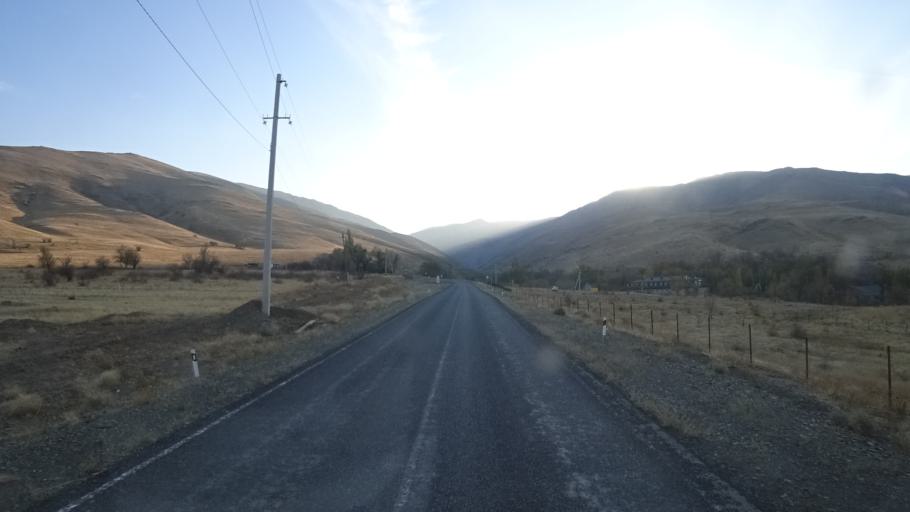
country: KZ
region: Zhambyl
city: Karatau
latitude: 42.9288
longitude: 70.6473
